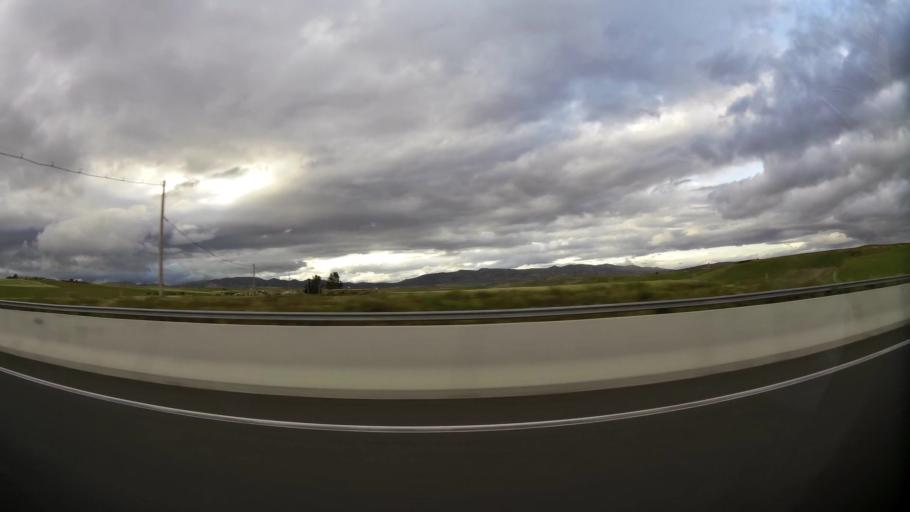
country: MA
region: Taza-Al Hoceima-Taounate
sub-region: Taza
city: Taza
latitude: 34.2538
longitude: -3.8853
